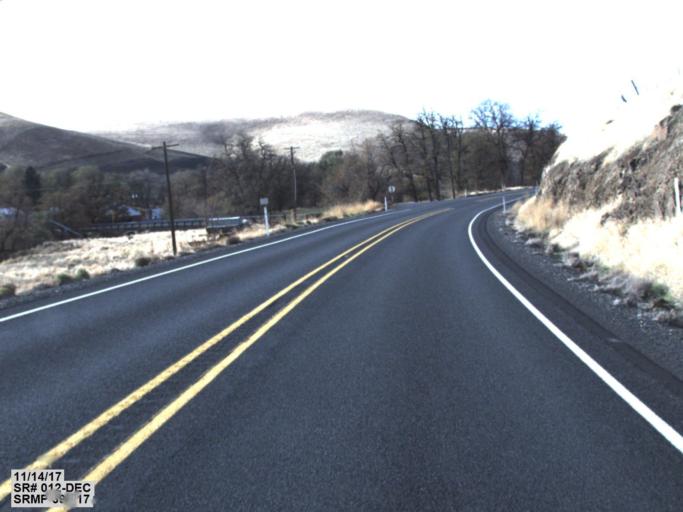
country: US
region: Washington
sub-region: Garfield County
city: Pomeroy
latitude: 46.4642
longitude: -117.7033
